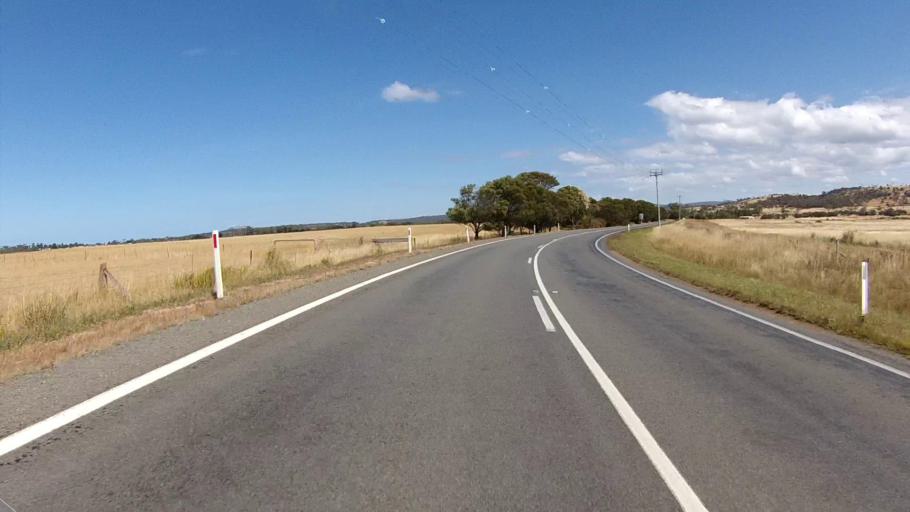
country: AU
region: Tasmania
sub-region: Break O'Day
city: St Helens
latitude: -42.1014
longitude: 148.0624
